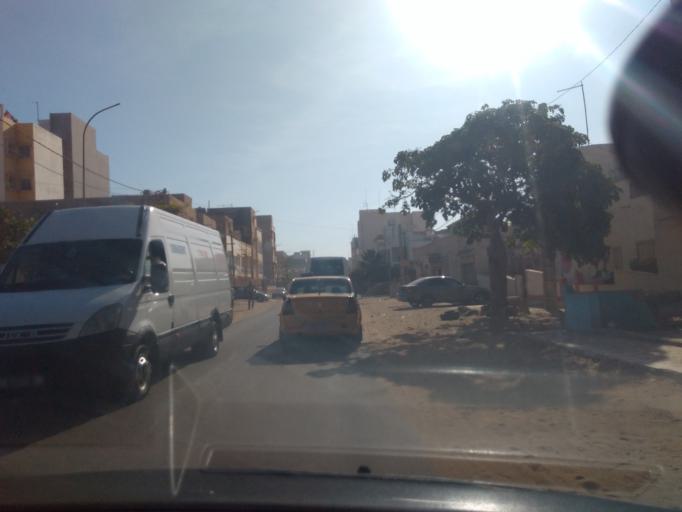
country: SN
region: Dakar
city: Grand Dakar
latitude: 14.7636
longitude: -17.4434
